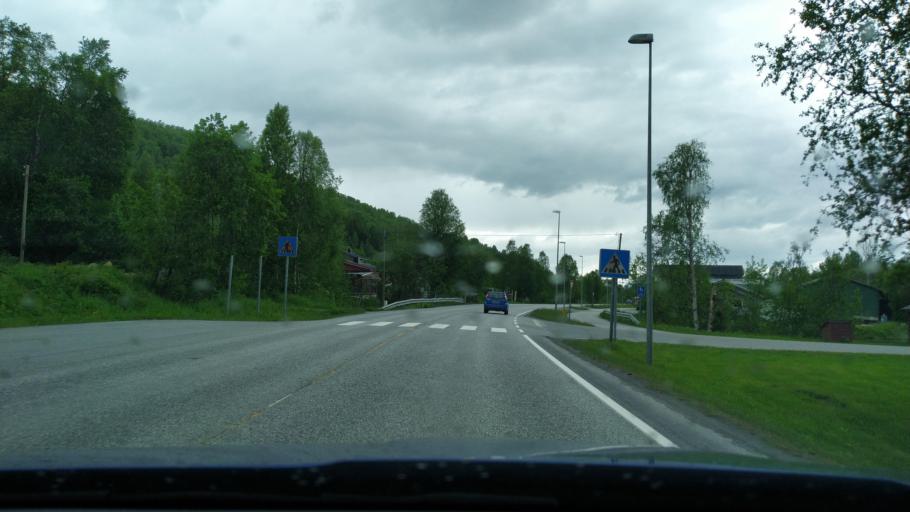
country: NO
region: Troms
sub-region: Malselv
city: Moen
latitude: 69.0307
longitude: 18.5020
